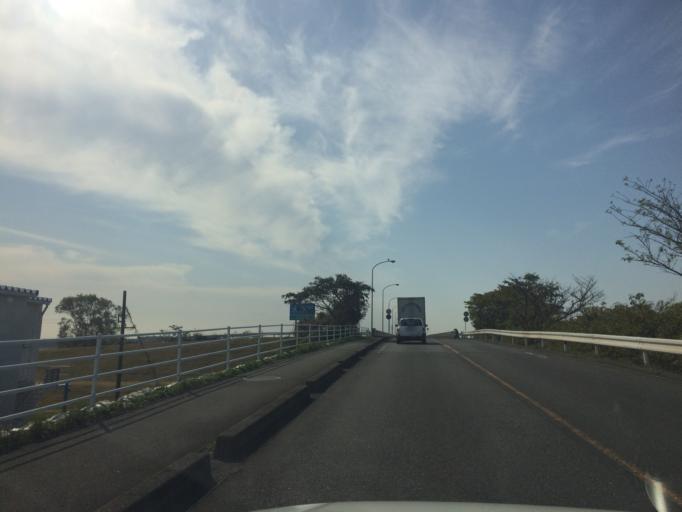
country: JP
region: Shizuoka
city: Fujieda
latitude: 34.7818
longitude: 138.2852
